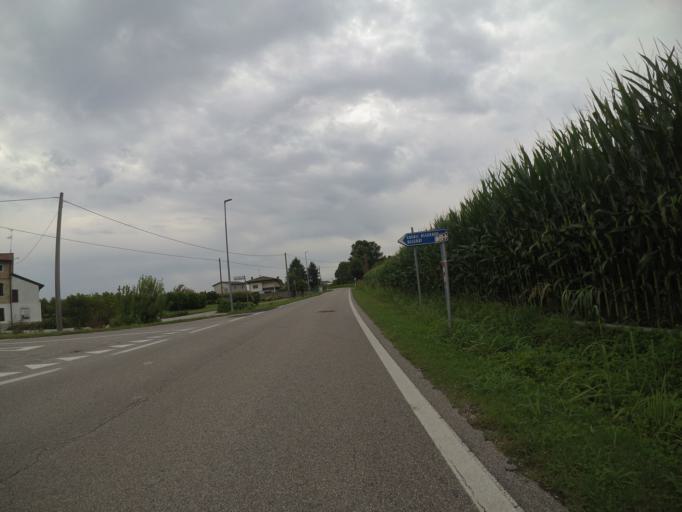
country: IT
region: Friuli Venezia Giulia
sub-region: Provincia di Udine
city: Camino al Tagliamento
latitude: 45.8946
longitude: 12.9535
